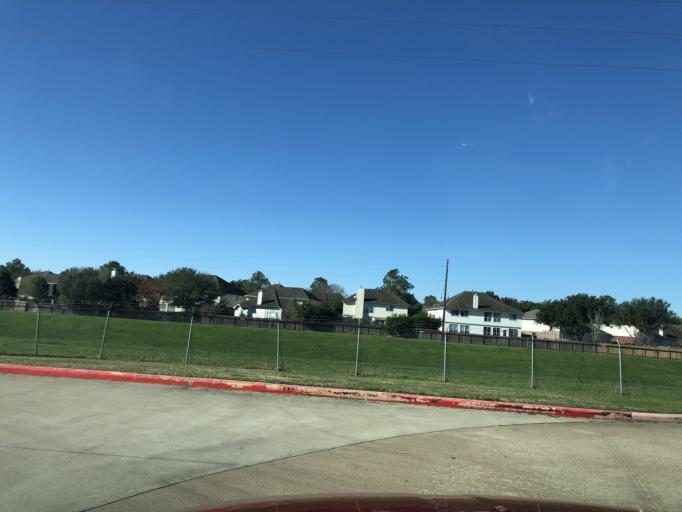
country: US
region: Texas
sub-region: Harris County
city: Oak Cliff Place
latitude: 29.9362
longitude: -95.6587
